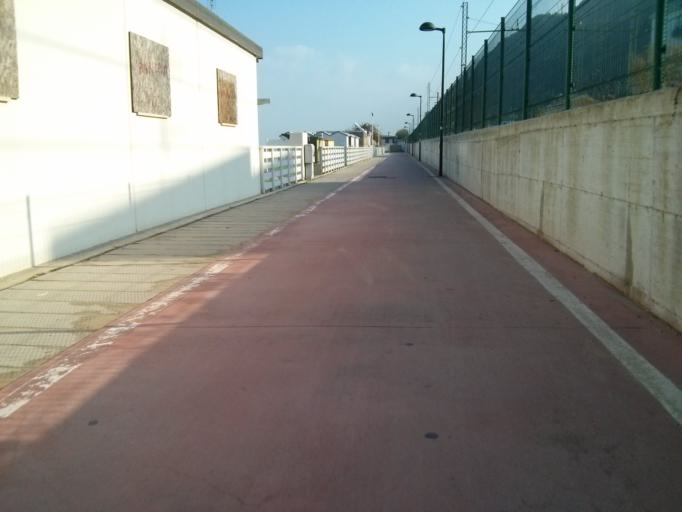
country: IT
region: The Marches
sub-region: Provincia di Pesaro e Urbino
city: Pesaro
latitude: 43.9050
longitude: 12.9306
